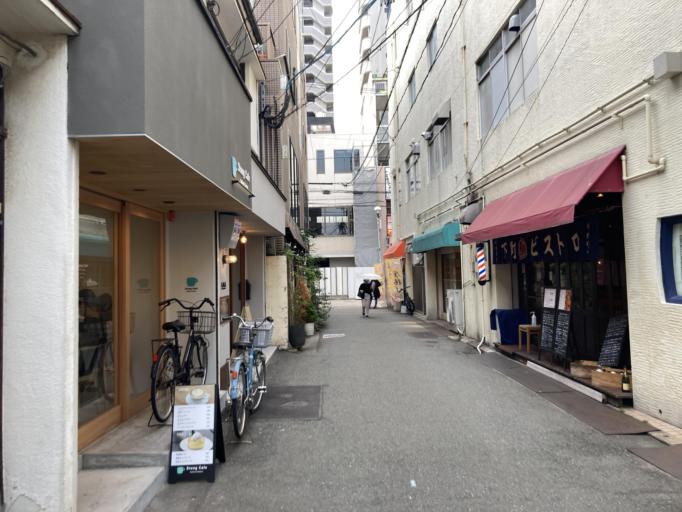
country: JP
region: Fukuoka
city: Fukuoka-shi
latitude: 33.5818
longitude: 130.3569
